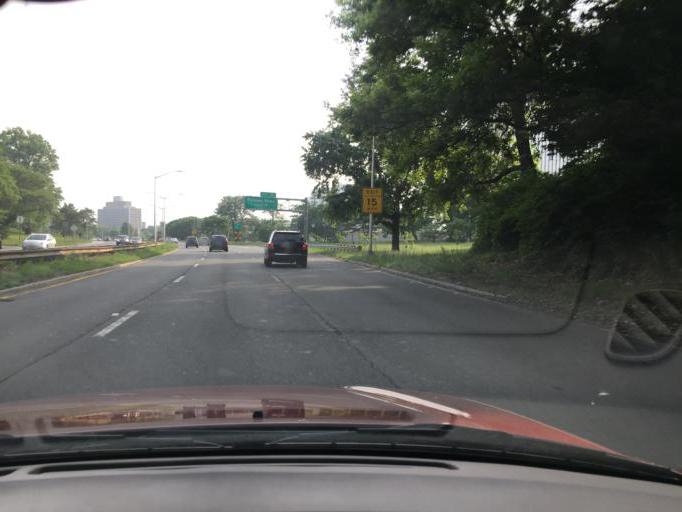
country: US
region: New York
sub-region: Bronx
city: Eastchester
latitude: 40.8559
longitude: -73.8332
